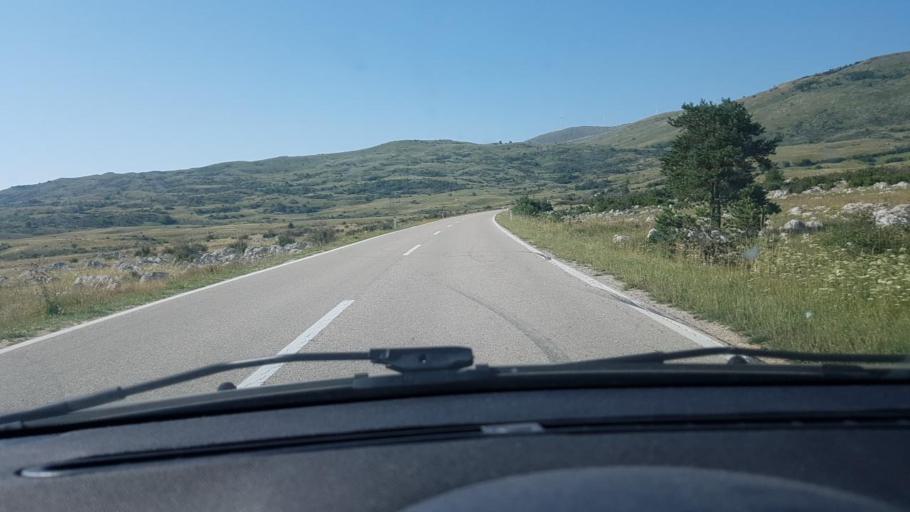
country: BA
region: Federation of Bosnia and Herzegovina
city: Tomislavgrad
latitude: 43.7926
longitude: 17.1706
